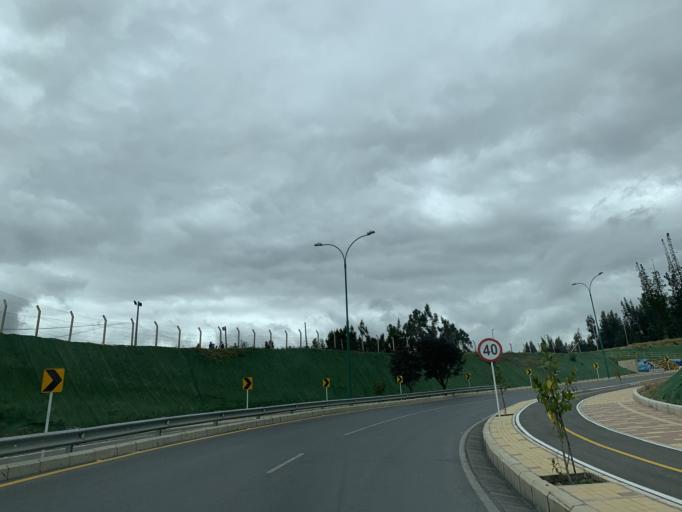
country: CO
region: Boyaca
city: Tunja
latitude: 5.5410
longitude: -73.3484
